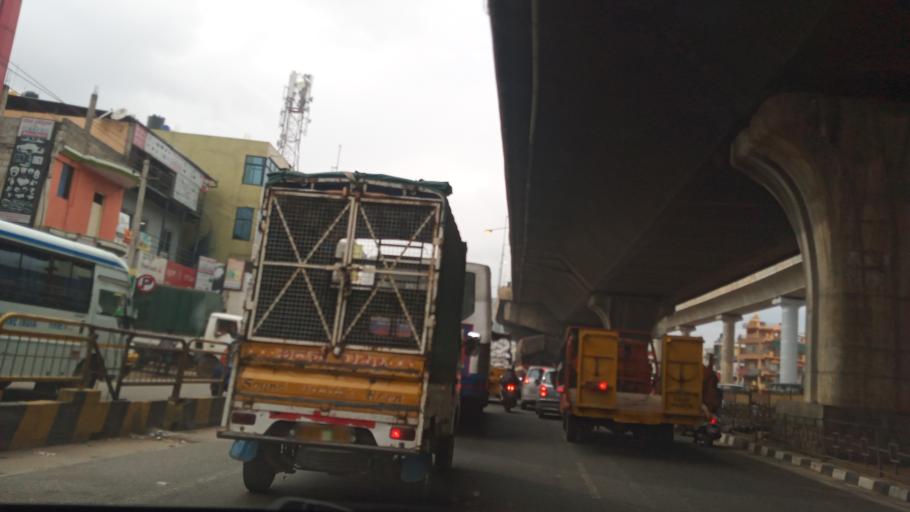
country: IN
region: Karnataka
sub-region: Bangalore Urban
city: Yelahanka
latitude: 13.0419
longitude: 77.5156
